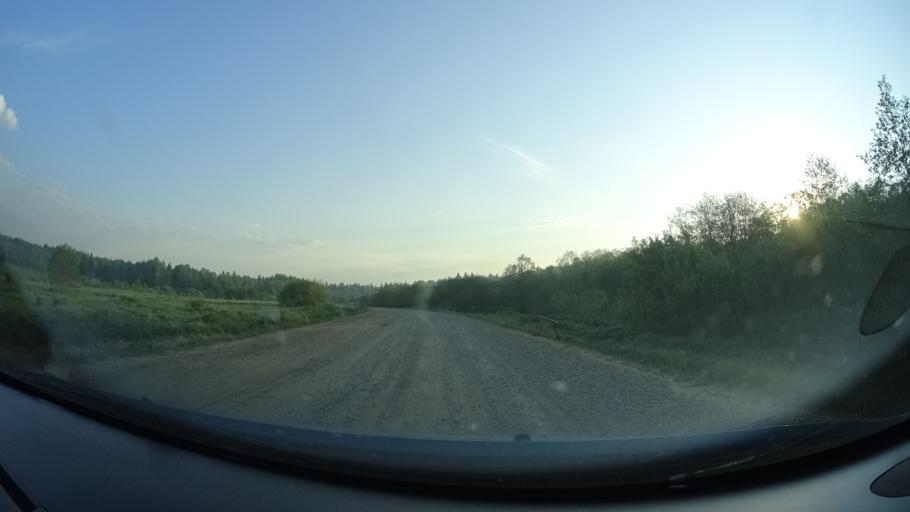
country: RU
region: Perm
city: Kuyeda
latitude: 56.6179
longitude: 55.7105
